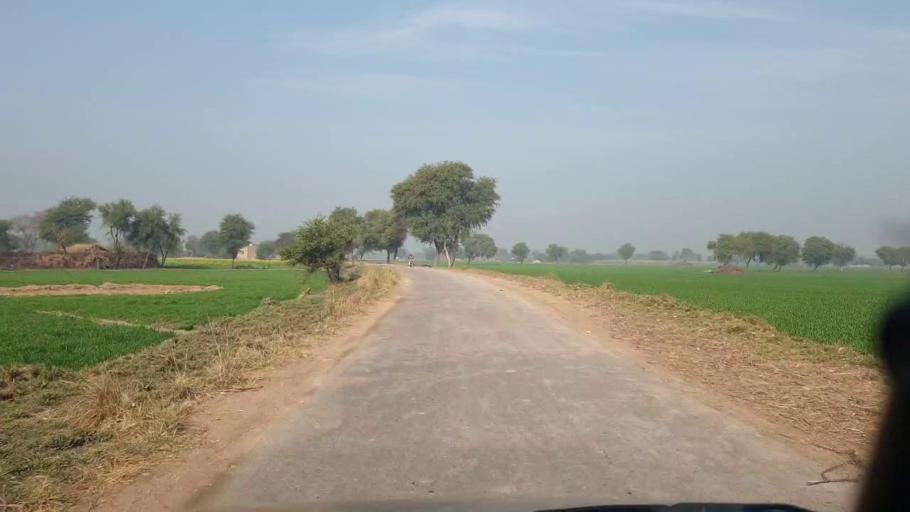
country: PK
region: Sindh
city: Shahdadpur
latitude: 26.0065
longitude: 68.5509
